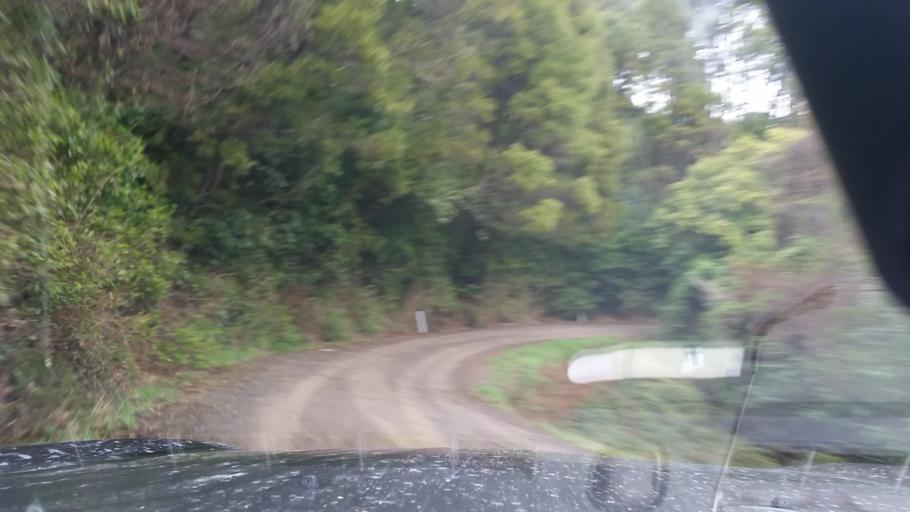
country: NZ
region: Nelson
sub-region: Nelson City
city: Nelson
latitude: -41.3621
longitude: 173.6104
